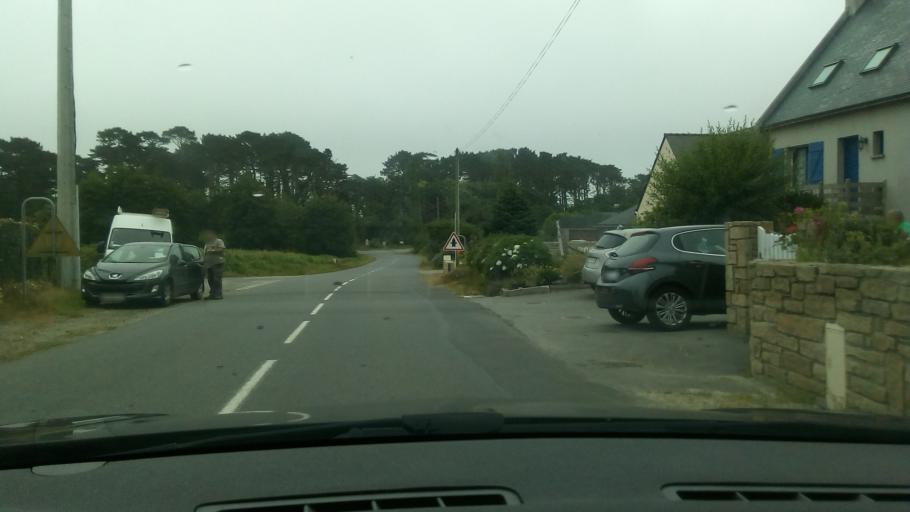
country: FR
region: Brittany
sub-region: Departement du Finistere
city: Le Conquet
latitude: 48.3741
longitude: -4.7474
